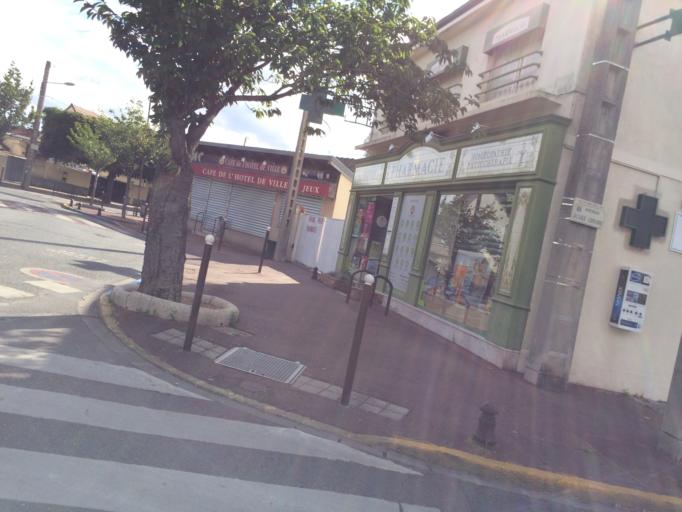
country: FR
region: Ile-de-France
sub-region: Departement de l'Essonne
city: Paray-Vieille-Poste
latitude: 48.7132
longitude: 2.3627
